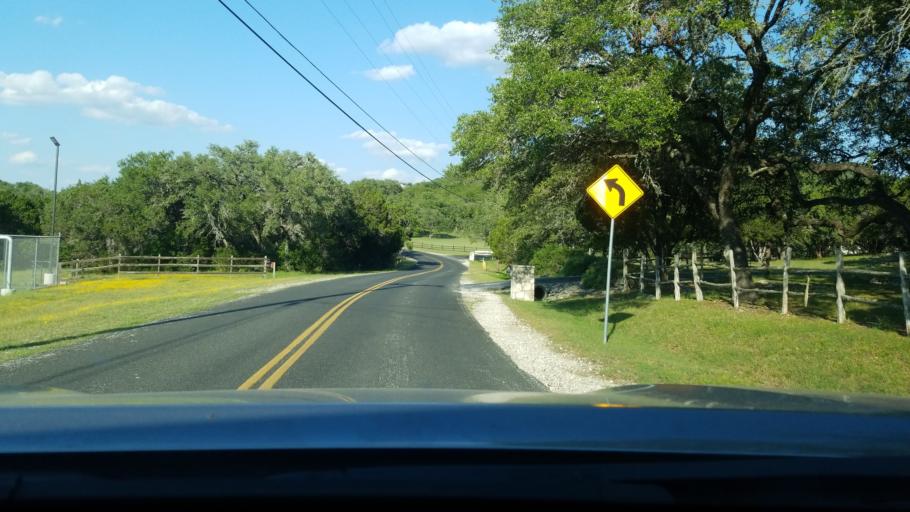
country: US
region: Texas
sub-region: Comal County
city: Bulverde
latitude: 29.7110
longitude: -98.4442
